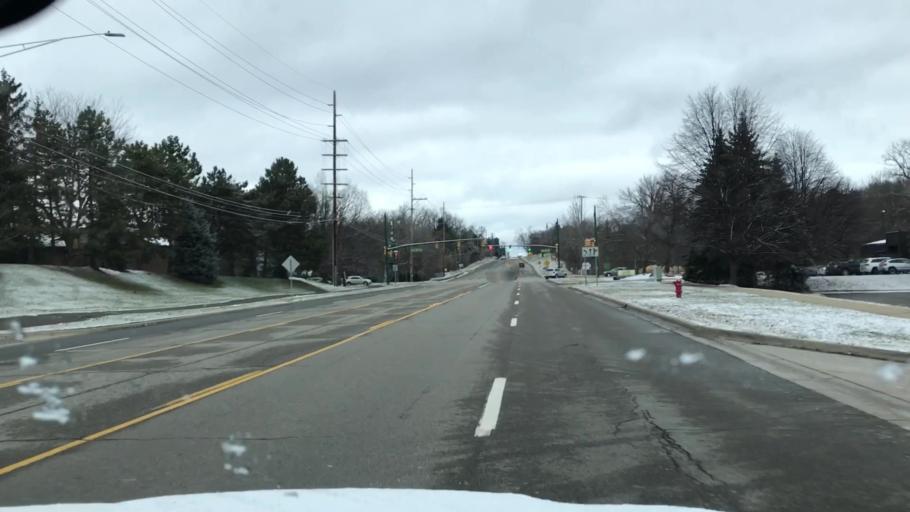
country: US
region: Michigan
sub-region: Wayne County
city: Northville
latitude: 42.4508
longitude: -83.4739
